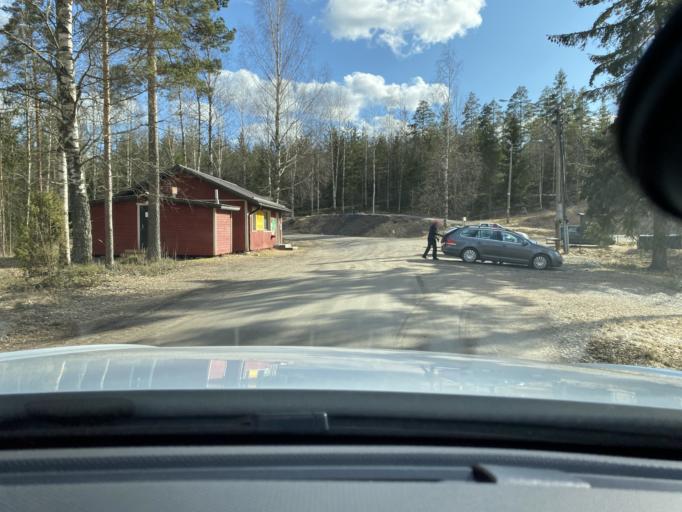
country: FI
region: Pirkanmaa
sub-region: Lounais-Pirkanmaa
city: Punkalaidun
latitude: 61.0922
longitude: 23.1364
